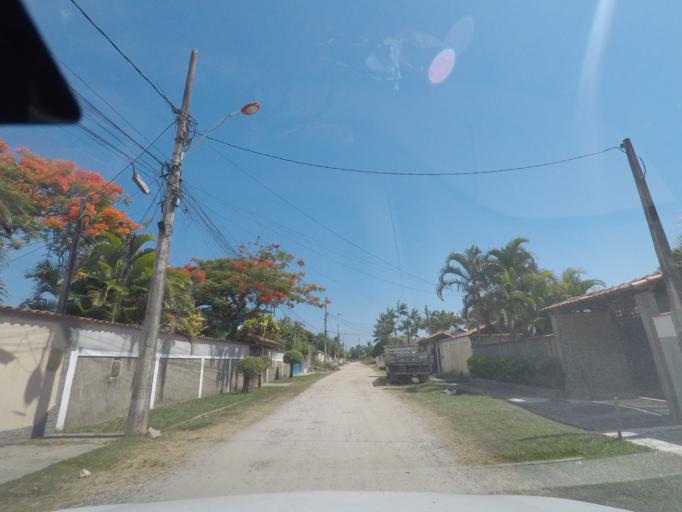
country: BR
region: Rio de Janeiro
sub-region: Marica
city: Marica
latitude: -22.9550
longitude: -42.9629
